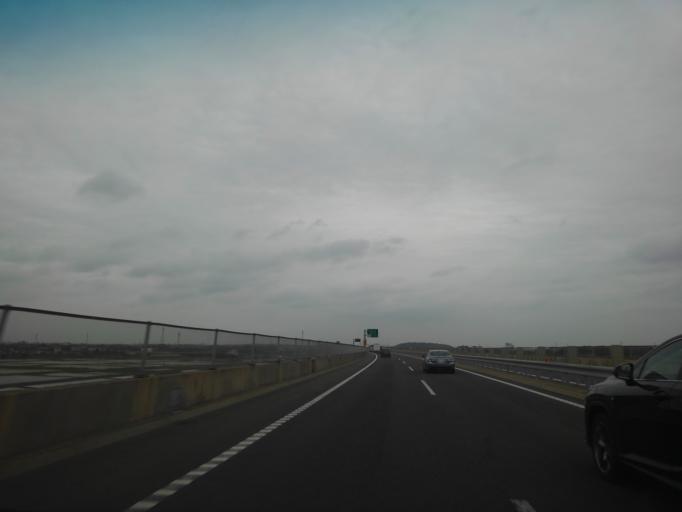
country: JP
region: Chiba
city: Kisarazu
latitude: 35.4036
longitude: 139.9656
